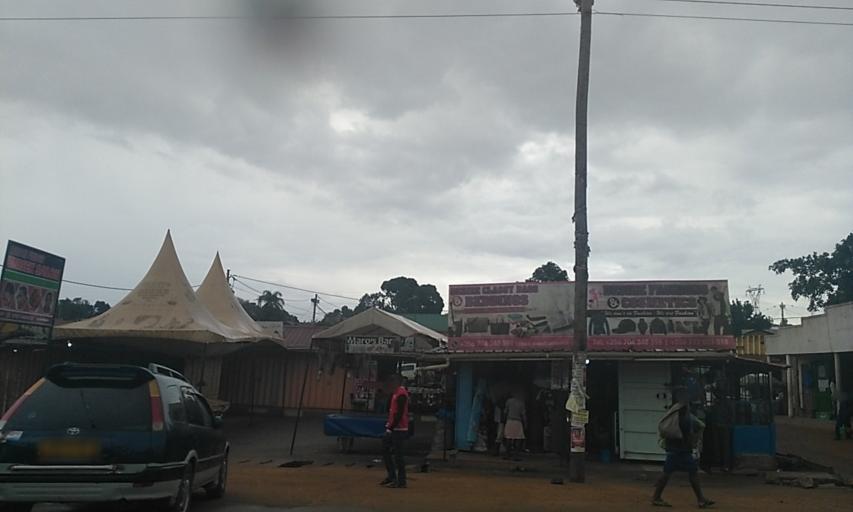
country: UG
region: Central Region
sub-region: Wakiso District
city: Kireka
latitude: 0.3457
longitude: 32.6460
